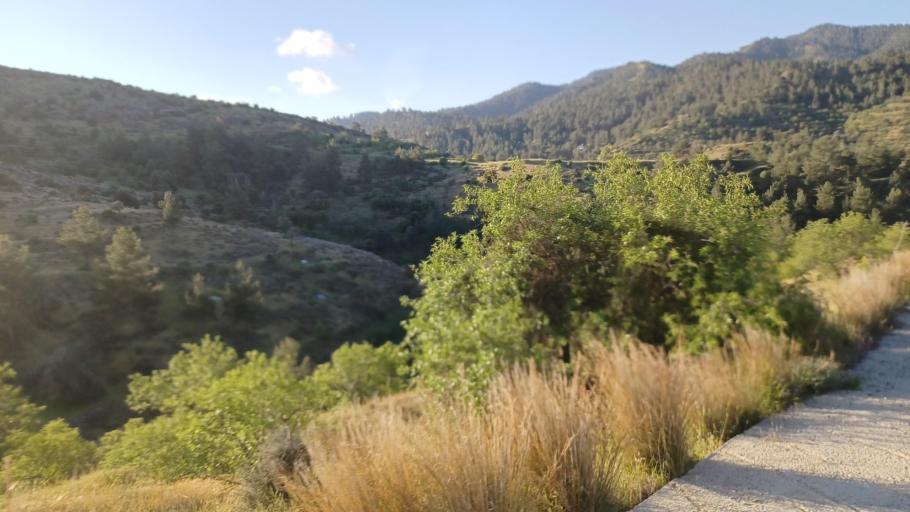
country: CY
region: Lefkosia
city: Peristerona
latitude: 35.0286
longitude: 33.0479
